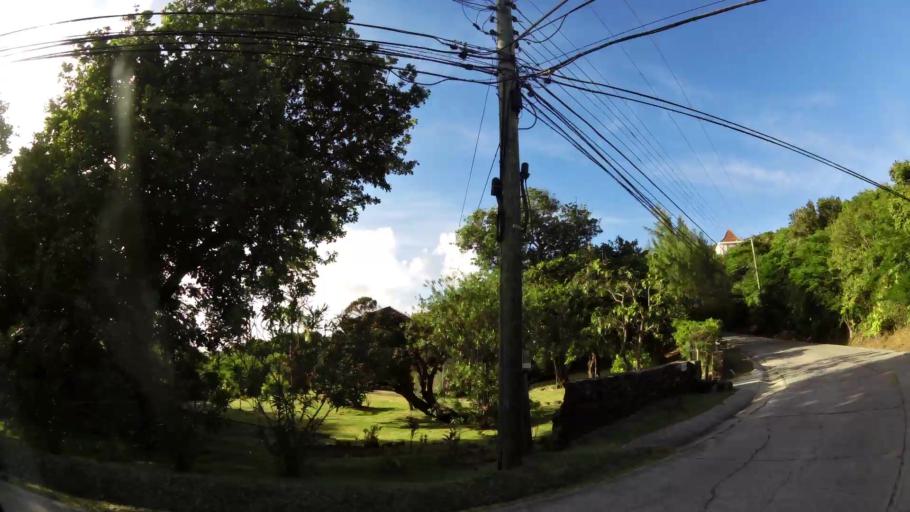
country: LC
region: Gros-Islet
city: Gros Islet
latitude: 14.1039
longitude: -60.9420
